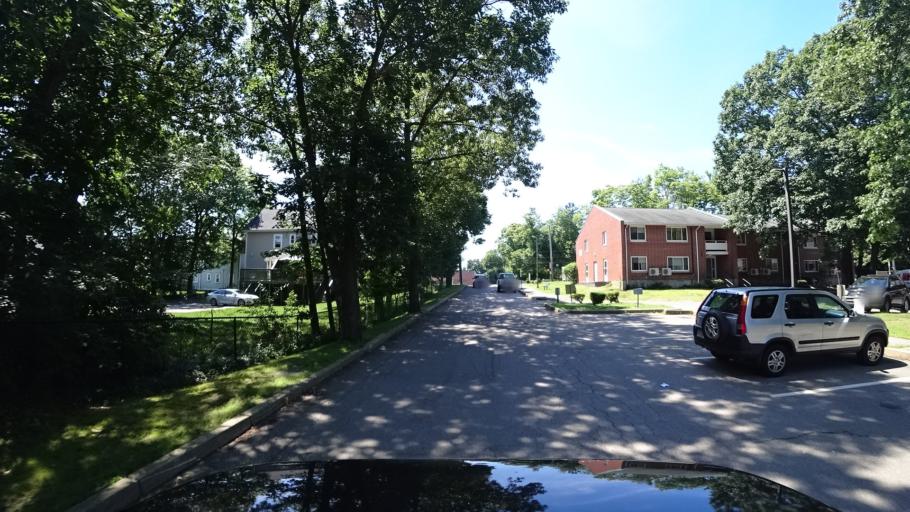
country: US
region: Massachusetts
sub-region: Norfolk County
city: Dedham
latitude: 42.2488
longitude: -71.1620
